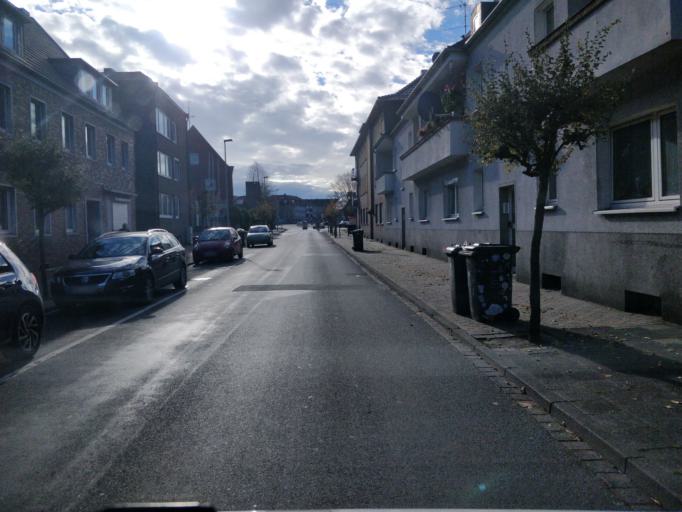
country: DE
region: North Rhine-Westphalia
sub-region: Regierungsbezirk Dusseldorf
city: Emmerich
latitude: 51.8372
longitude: 6.2472
